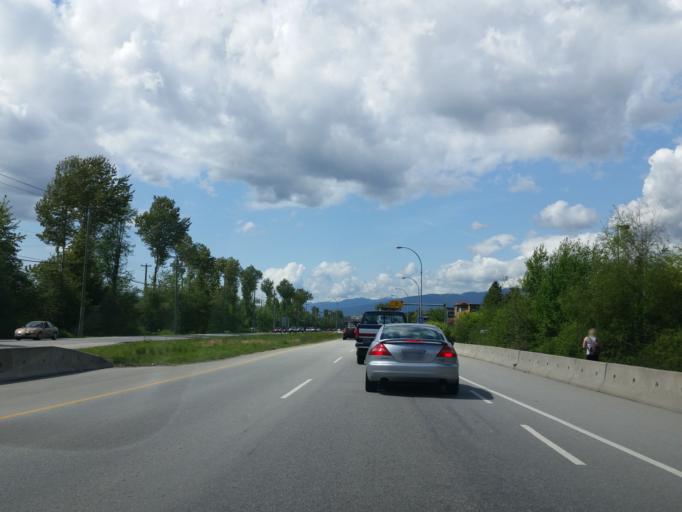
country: CA
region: British Columbia
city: Coquitlam
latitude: 49.2544
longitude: -122.7447
